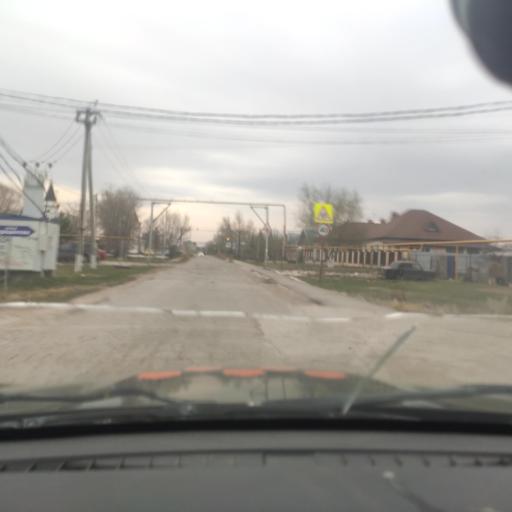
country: RU
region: Samara
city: Podstepki
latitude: 53.5133
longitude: 49.1273
